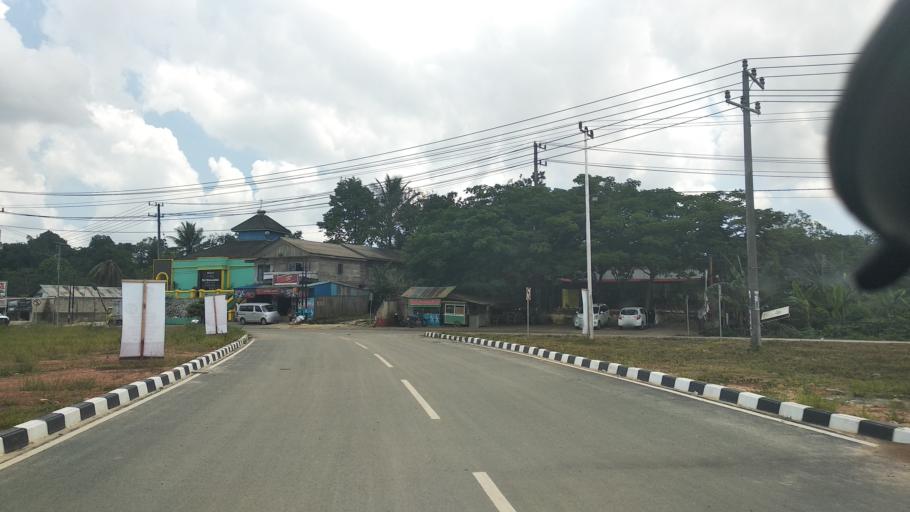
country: ID
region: East Kalimantan
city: Samarinda
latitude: -0.3731
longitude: 117.2645
